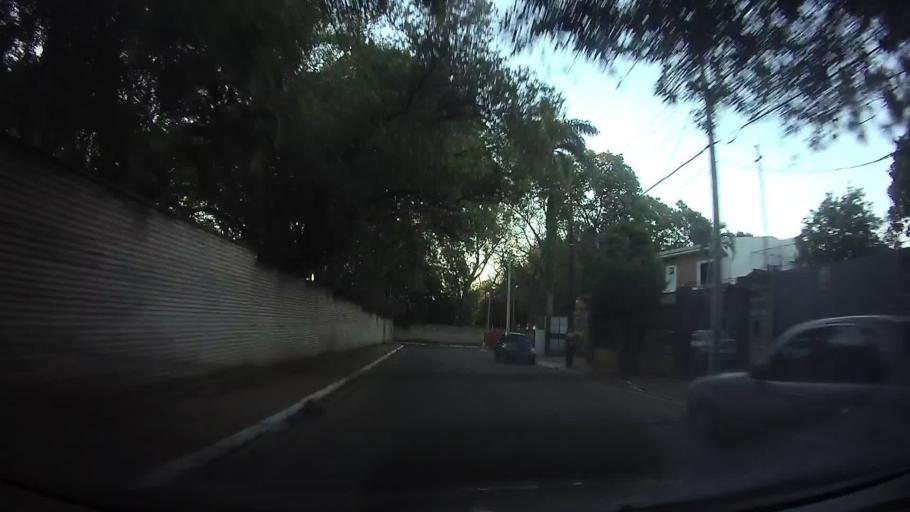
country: PY
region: Central
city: Fernando de la Mora
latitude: -25.3303
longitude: -57.5456
